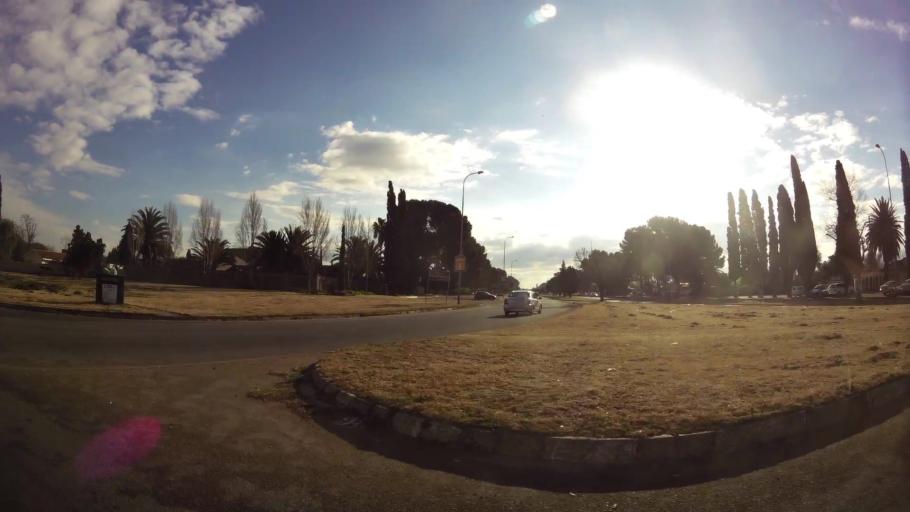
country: ZA
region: Orange Free State
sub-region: Lejweleputswa District Municipality
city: Welkom
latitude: -27.9870
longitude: 26.7554
